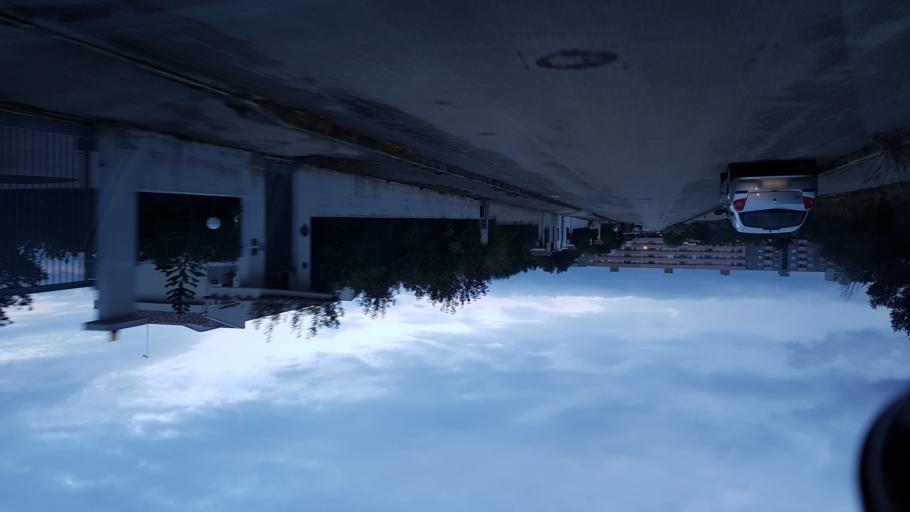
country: IT
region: Apulia
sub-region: Provincia di Taranto
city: Paolo VI
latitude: 40.5284
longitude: 17.2847
